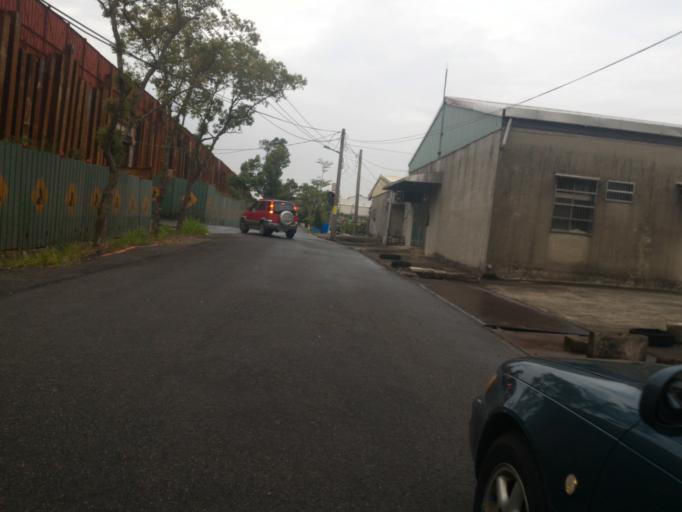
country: TW
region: Taiwan
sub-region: Taoyuan
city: Taoyuan
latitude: 24.9502
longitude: 121.3751
